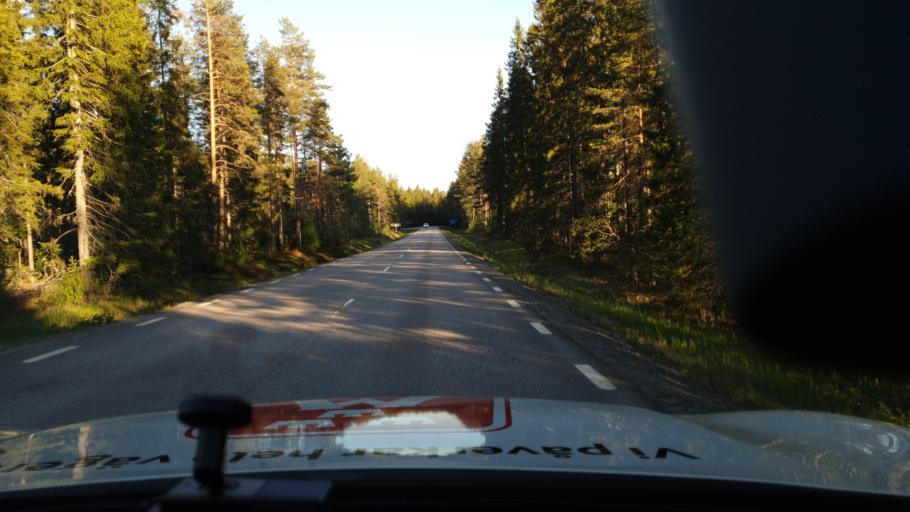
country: SE
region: Vaesterbotten
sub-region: Umea Kommun
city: Ersmark
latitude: 63.9484
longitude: 20.3011
